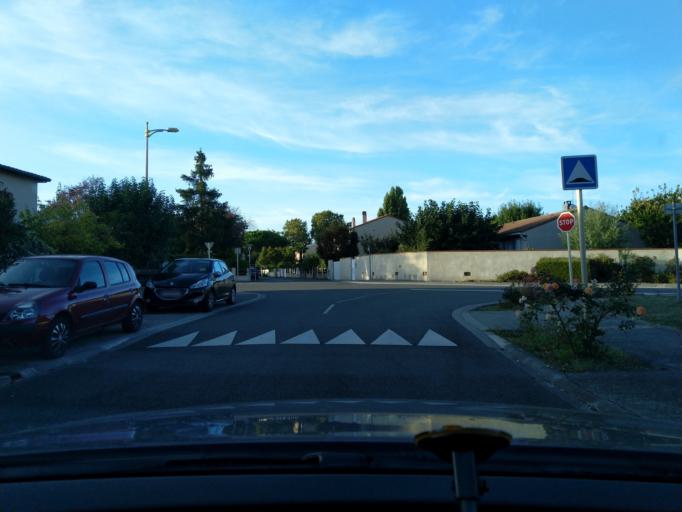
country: FR
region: Midi-Pyrenees
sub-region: Departement de la Haute-Garonne
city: Tournefeuille
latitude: 43.5769
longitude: 1.3294
